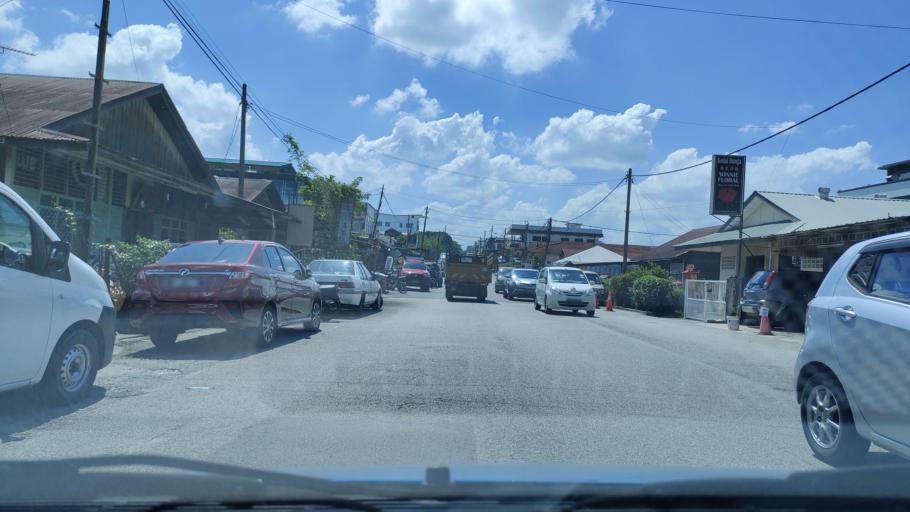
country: MY
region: Selangor
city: Kampong Baharu Balakong
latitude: 3.0219
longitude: 101.7042
